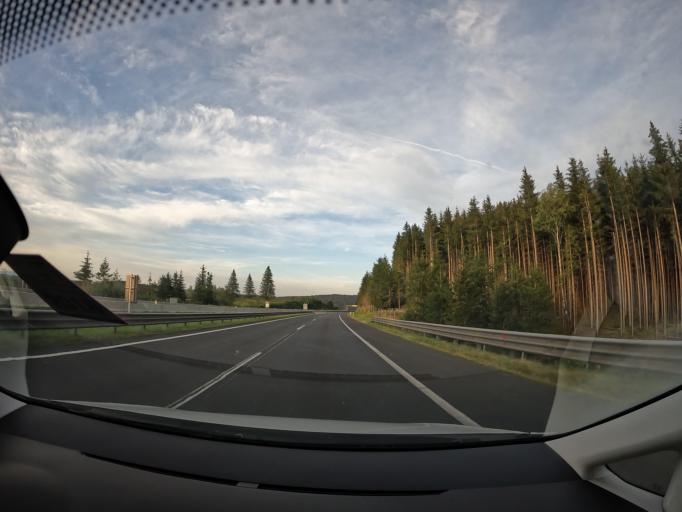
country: AT
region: Styria
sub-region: Politischer Bezirk Voitsberg
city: Modriach
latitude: 46.9549
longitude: 15.0158
